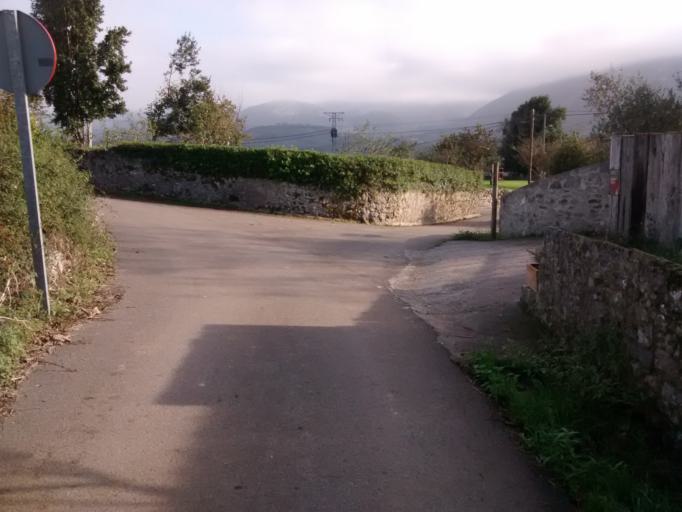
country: ES
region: Asturias
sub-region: Province of Asturias
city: Colunga
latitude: 43.4698
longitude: -5.2389
